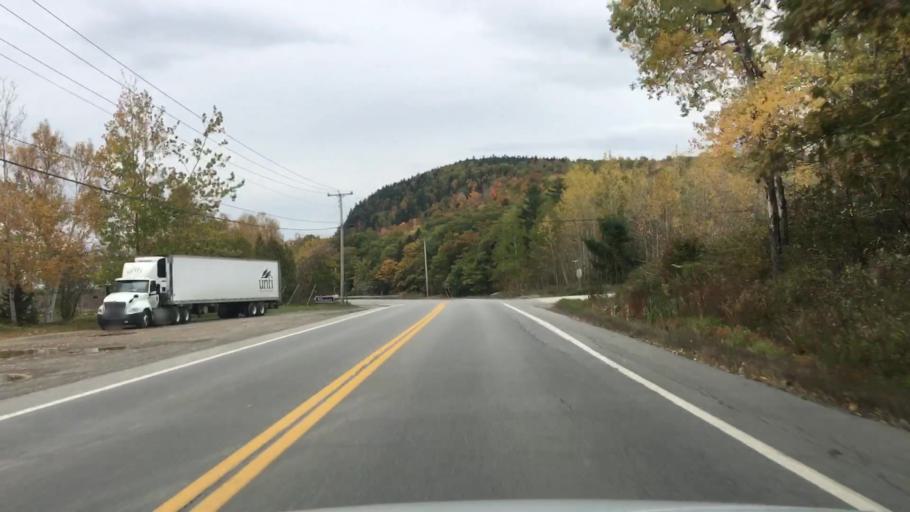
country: US
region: Maine
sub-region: Waldo County
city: Frankfort
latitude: 44.5914
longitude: -68.8658
